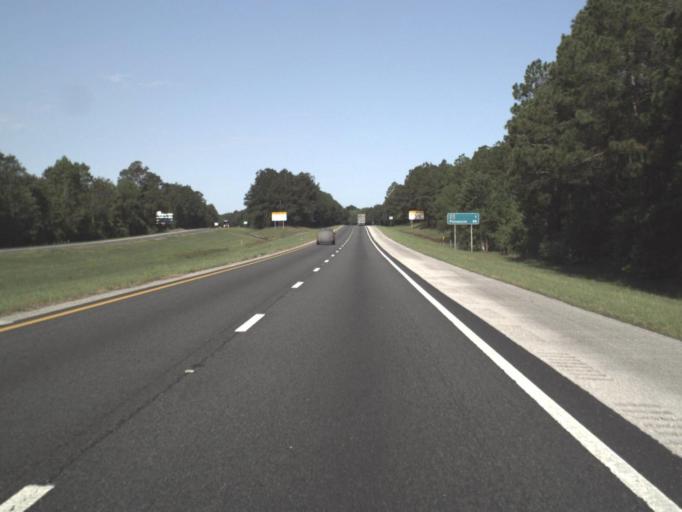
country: US
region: Florida
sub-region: Holmes County
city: Bonifay
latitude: 30.7634
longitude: -85.7023
